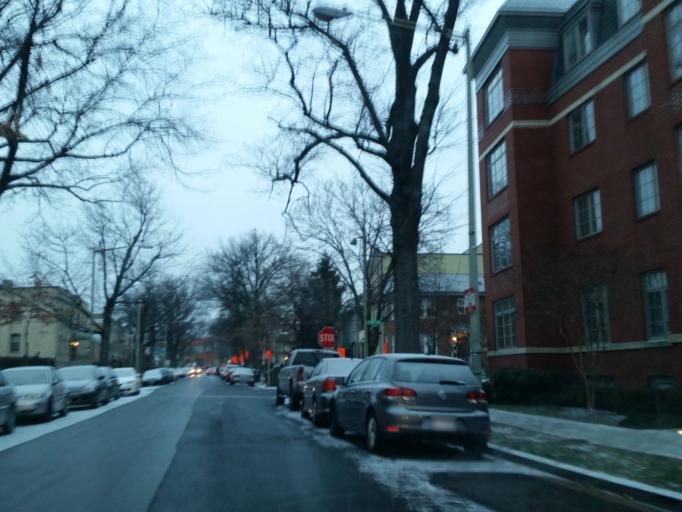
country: US
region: Washington, D.C.
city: Washington, D.C.
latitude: 38.9176
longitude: -77.0145
